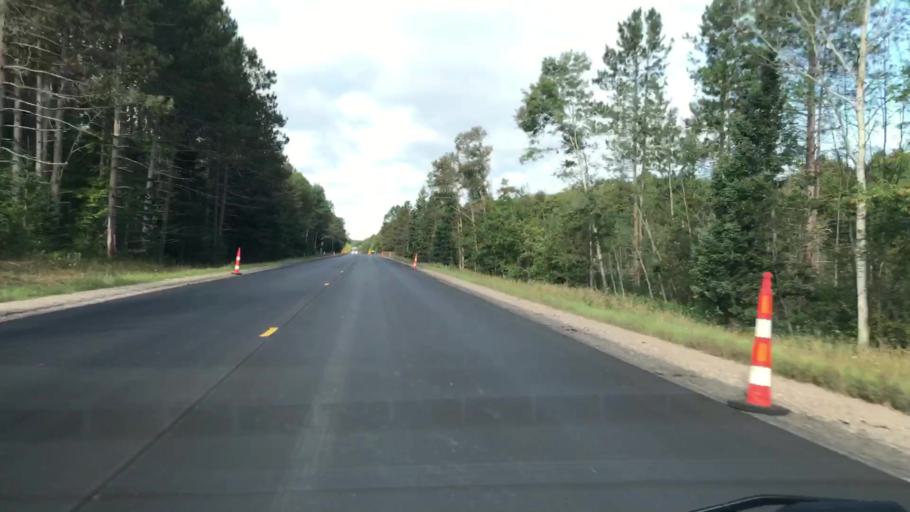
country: US
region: Michigan
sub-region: Luce County
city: Newberry
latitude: 46.3464
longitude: -85.0144
